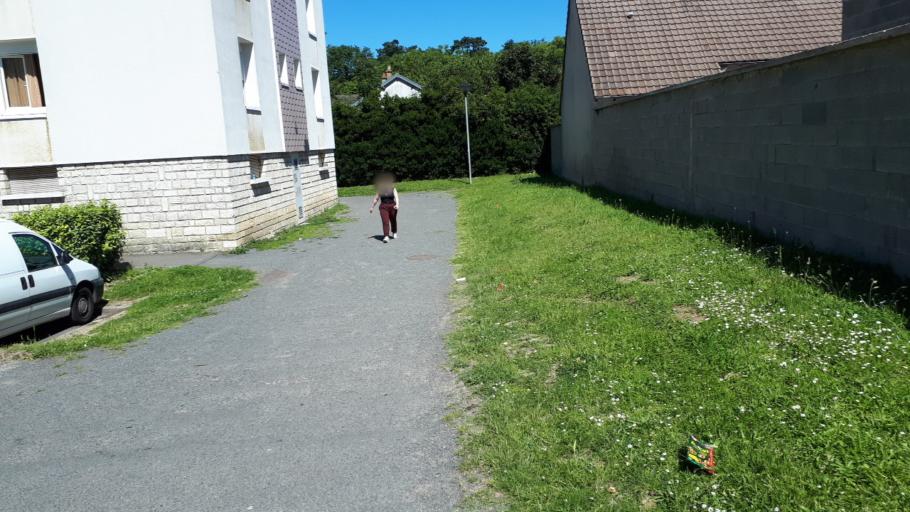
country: FR
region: Centre
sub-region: Departement d'Indre-et-Loire
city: Joue-les-Tours
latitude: 47.3463
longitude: 0.6640
